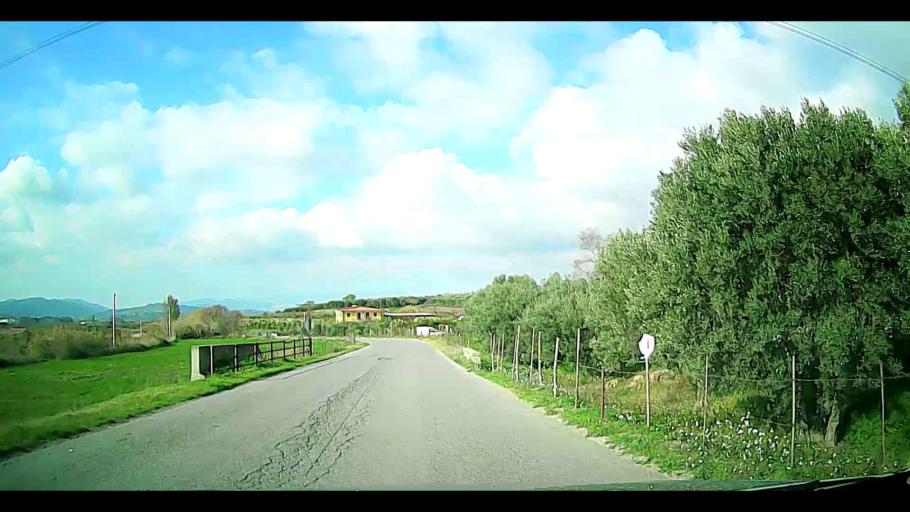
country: IT
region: Calabria
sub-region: Provincia di Crotone
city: Rocca di Neto
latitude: 39.1814
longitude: 17.0382
